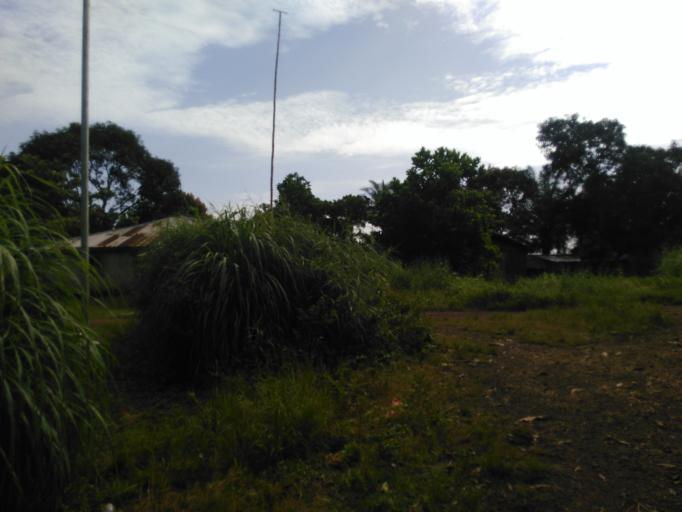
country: SL
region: Southern Province
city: Rotifunk
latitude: 8.4831
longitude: -12.7567
